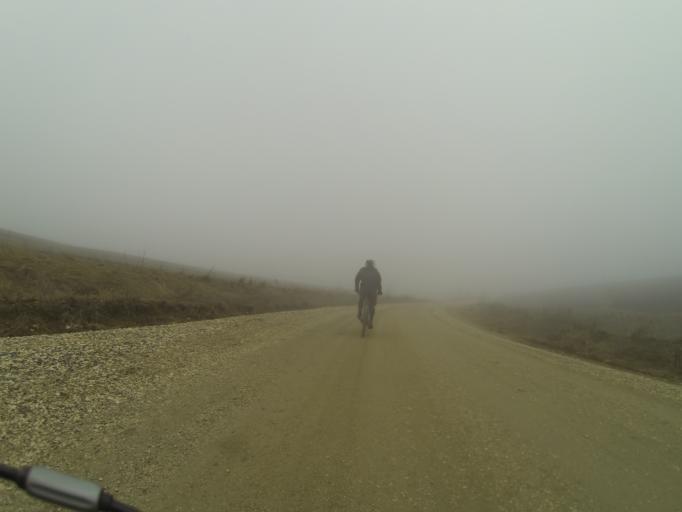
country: RO
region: Mehedinti
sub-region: Comuna Balacita
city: Gvardinita
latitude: 44.4256
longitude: 23.1298
